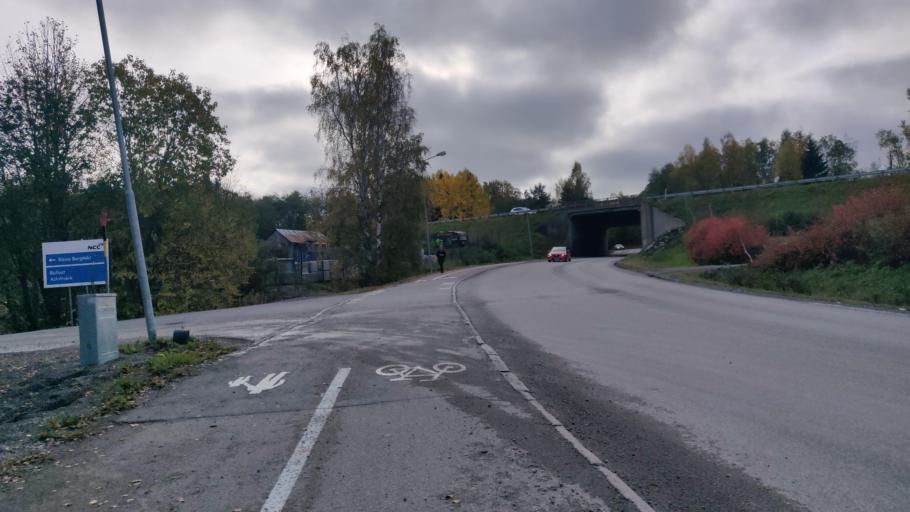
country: SE
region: Vaesternorrland
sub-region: Sundsvalls Kommun
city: Sundsbruk
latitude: 62.4350
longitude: 17.3425
